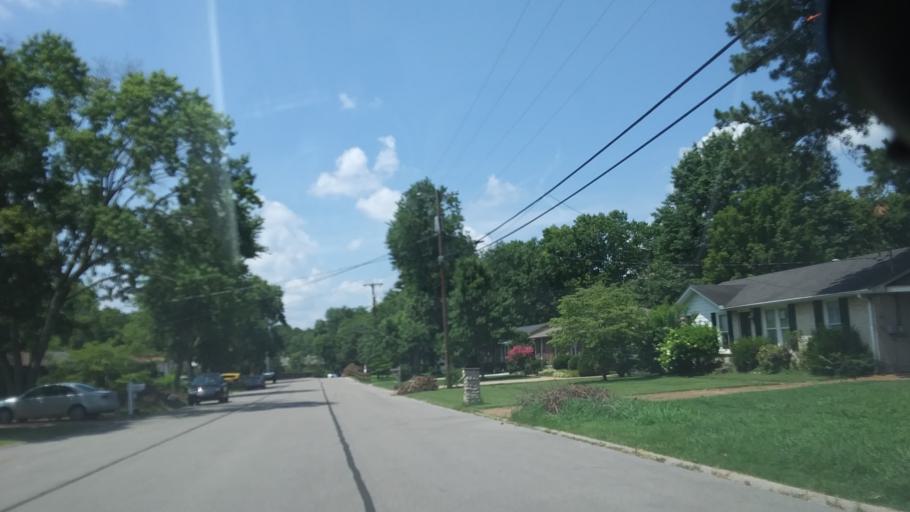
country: US
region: Tennessee
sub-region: Davidson County
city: Belle Meade
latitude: 36.0868
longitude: -86.9414
